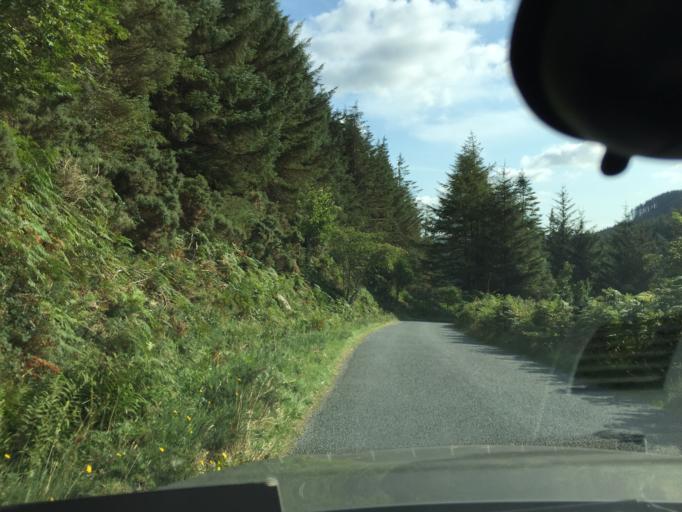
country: IE
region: Leinster
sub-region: Wicklow
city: Rathdrum
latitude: 53.0568
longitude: -6.3312
